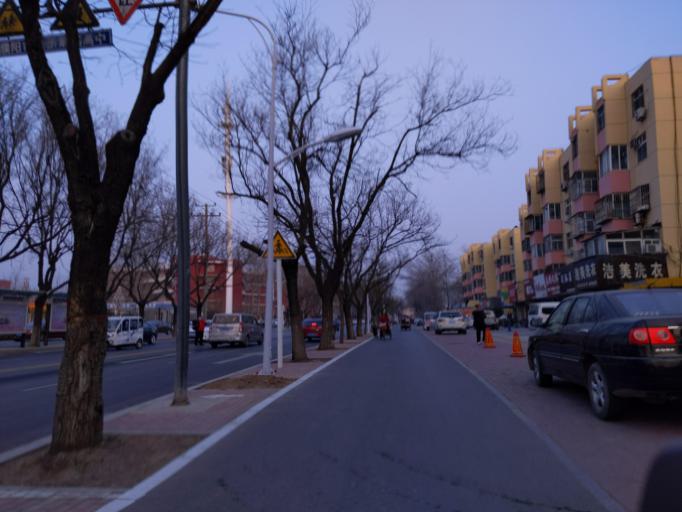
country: CN
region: Henan Sheng
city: Zhongyuanlu
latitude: 35.7693
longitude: 115.0946
